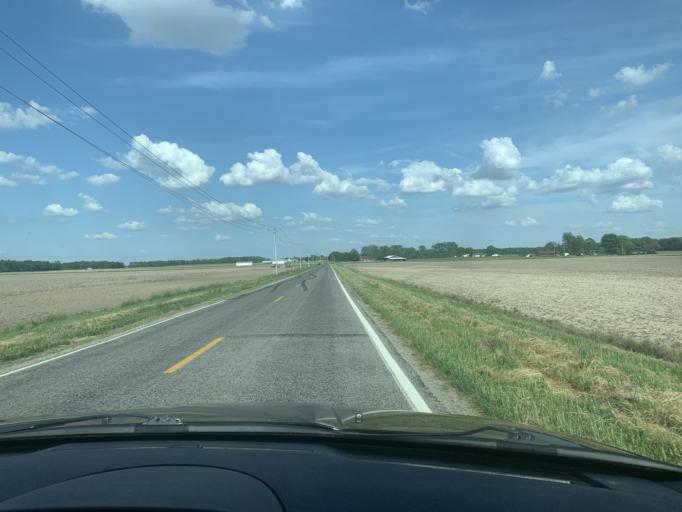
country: US
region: Ohio
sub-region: Logan County
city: De Graff
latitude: 40.2438
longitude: -84.0118
